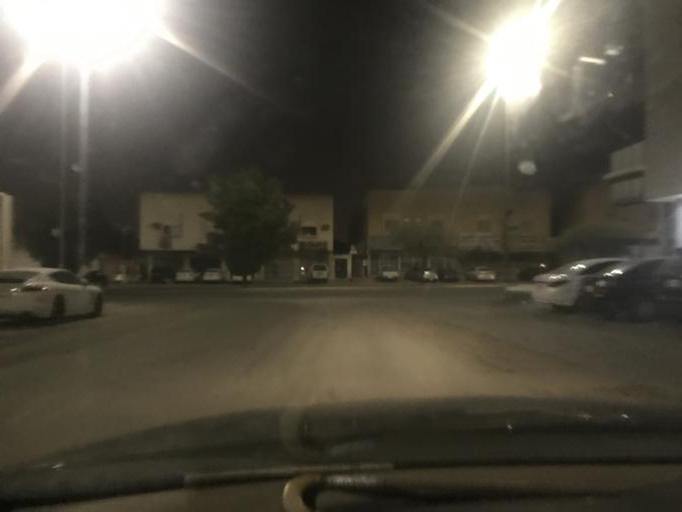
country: SA
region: Ar Riyad
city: Riyadh
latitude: 24.7254
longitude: 46.7656
